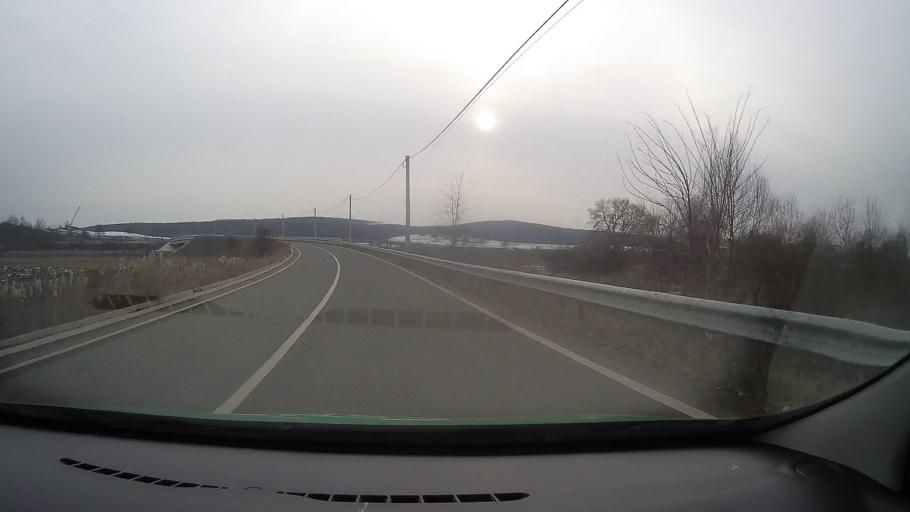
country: RO
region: Hunedoara
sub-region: Comuna Turdas
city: Turdas
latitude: 45.8424
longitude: 23.1197
